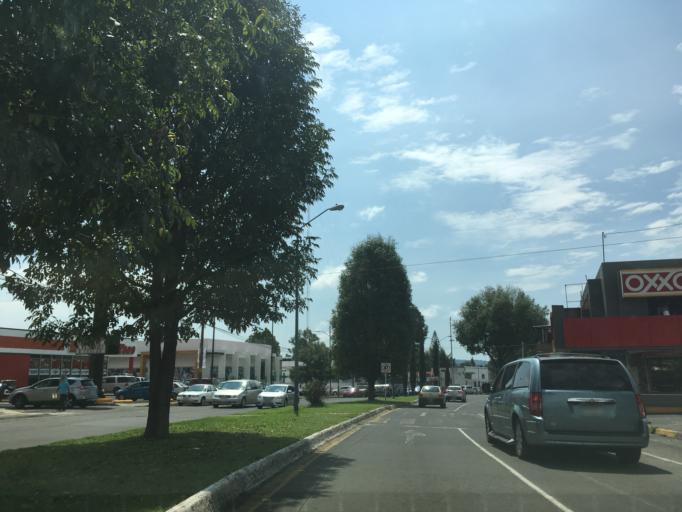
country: MX
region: Michoacan
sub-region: Uruapan
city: Uruapan
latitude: 19.4235
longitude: -102.0478
